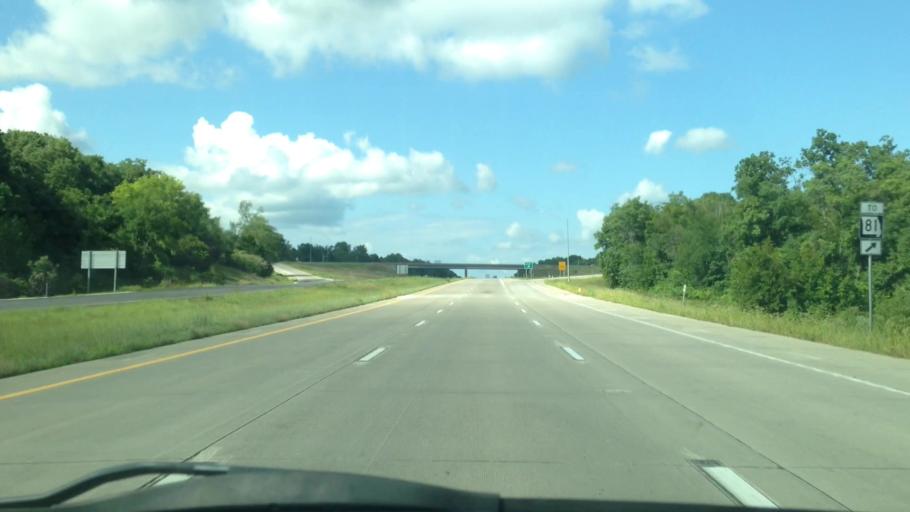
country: US
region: Missouri
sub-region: Lewis County
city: Canton
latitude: 40.1294
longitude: -91.5409
